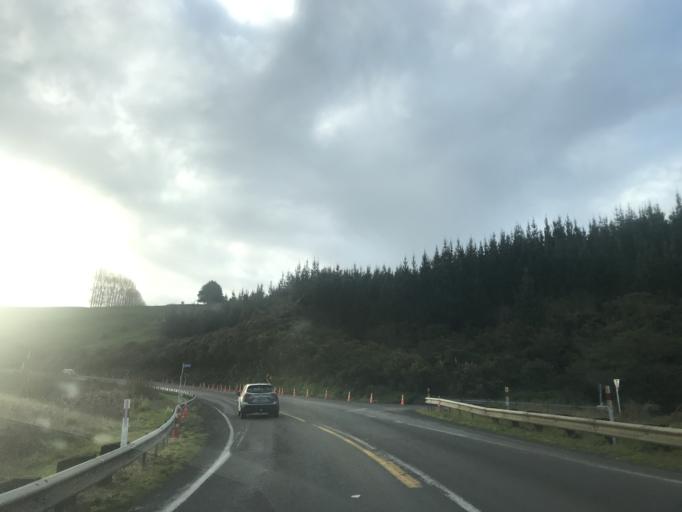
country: NZ
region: Bay of Plenty
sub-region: Western Bay of Plenty District
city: Waihi Beach
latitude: -37.4531
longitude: 175.8923
